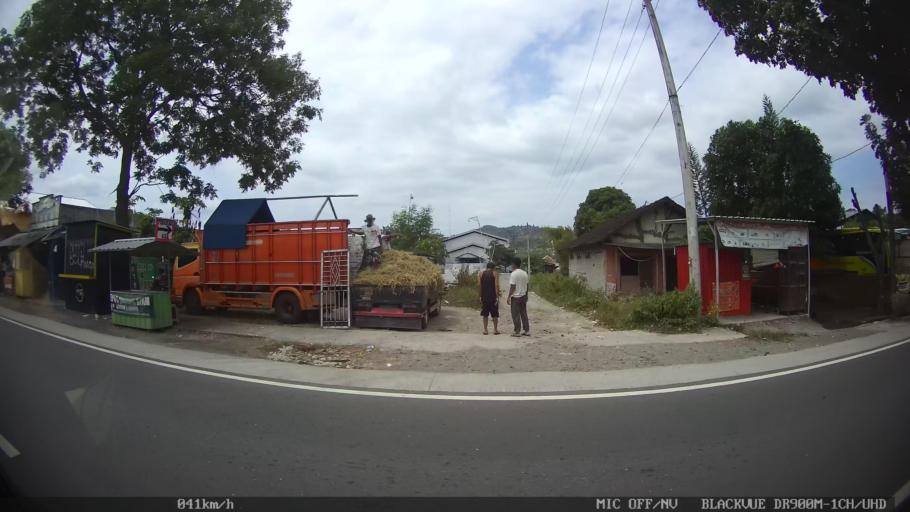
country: ID
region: Central Java
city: Candi Prambanan
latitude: -7.7821
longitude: 110.4826
